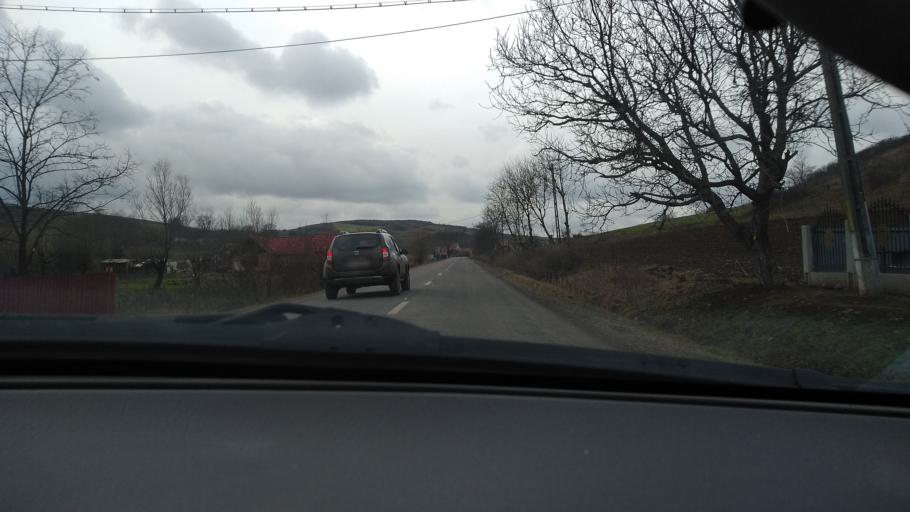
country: RO
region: Mures
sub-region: Comuna Galesti
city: Galesti
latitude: 46.5437
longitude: 24.7437
